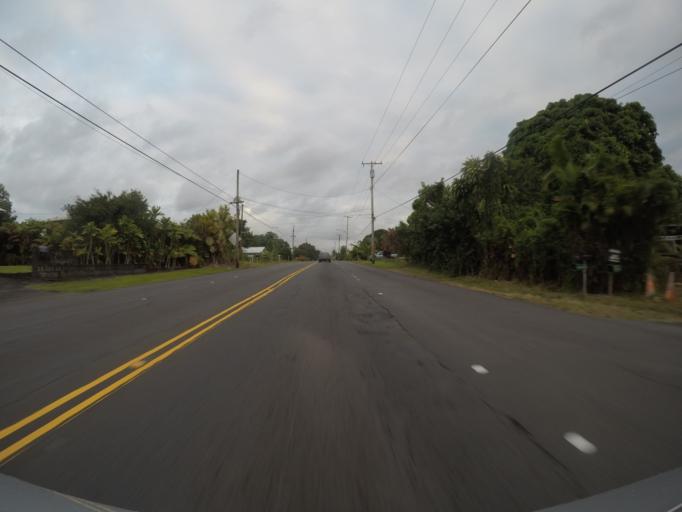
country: US
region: Hawaii
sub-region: Hawaii County
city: Hilo
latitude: 19.6825
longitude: -155.0674
